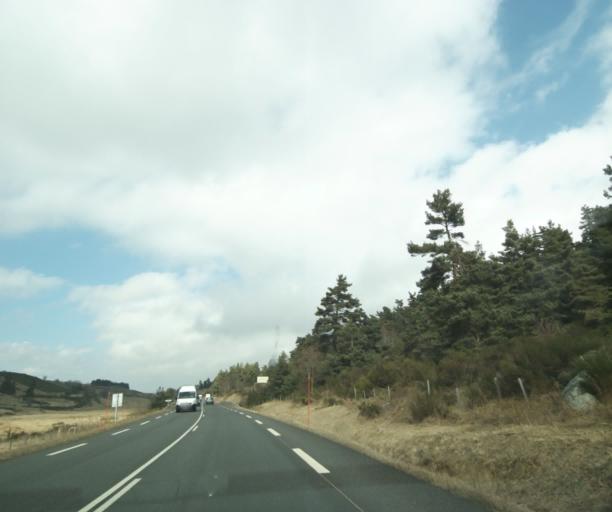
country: FR
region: Languedoc-Roussillon
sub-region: Departement de la Lozere
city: Mende
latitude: 44.6077
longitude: 3.6759
